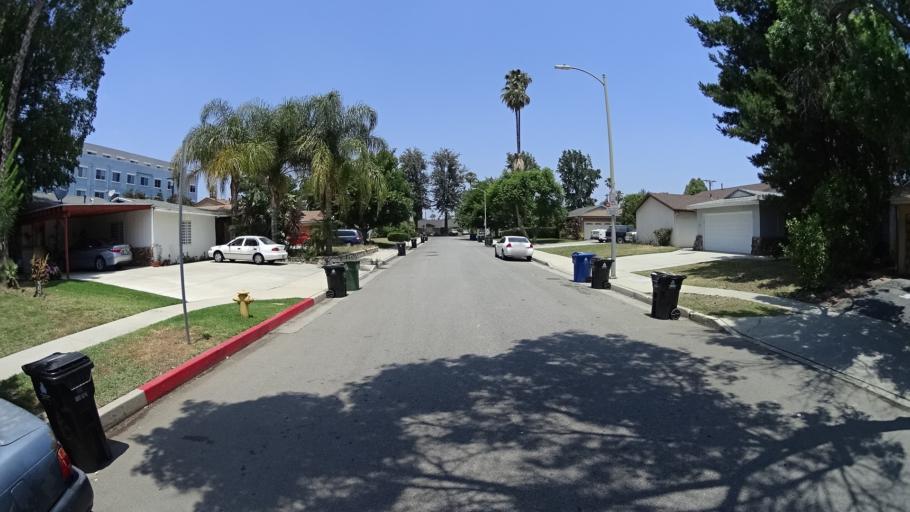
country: US
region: California
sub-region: Los Angeles County
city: Van Nuys
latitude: 34.1966
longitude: -118.4647
